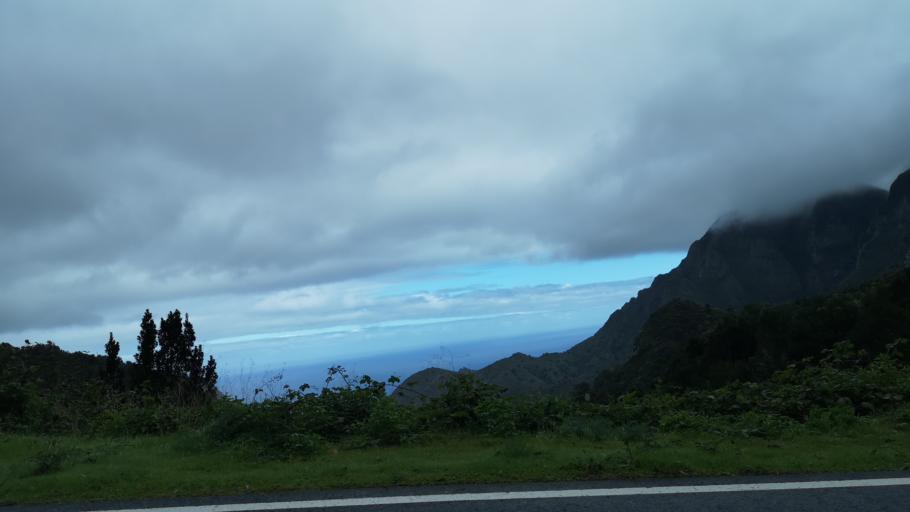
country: ES
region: Canary Islands
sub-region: Provincia de Santa Cruz de Tenerife
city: Hermigua
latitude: 28.1312
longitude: -17.2039
